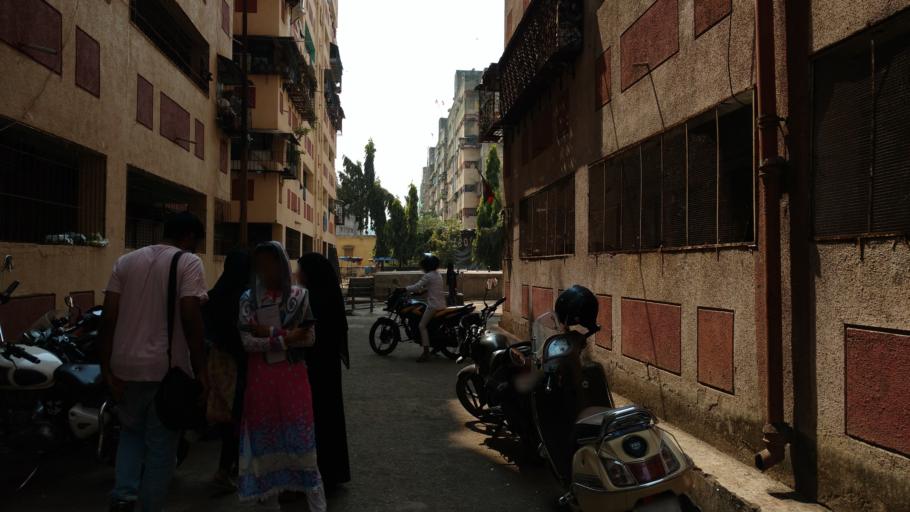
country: IN
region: Maharashtra
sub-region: Mumbai Suburban
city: Mumbai
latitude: 19.0653
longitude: 72.9168
